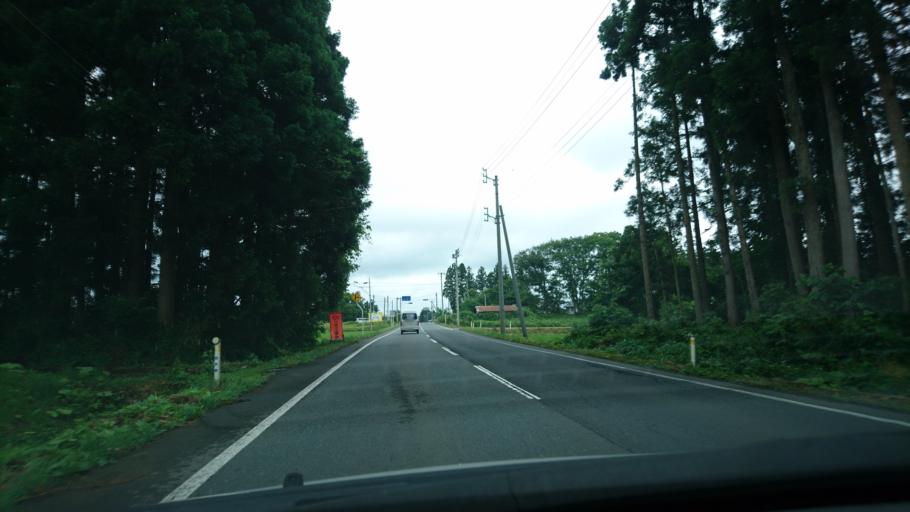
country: JP
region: Iwate
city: Mizusawa
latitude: 39.1179
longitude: 141.0528
